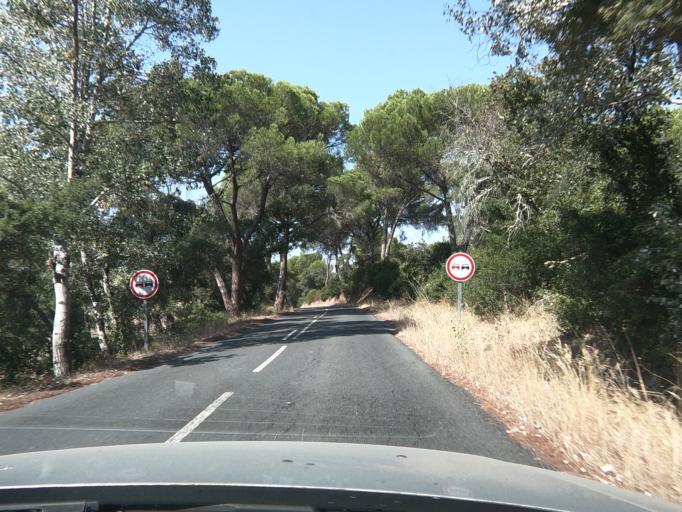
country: PT
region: Setubal
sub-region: Alcacer do Sal
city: Alcacer do Sal
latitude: 38.3077
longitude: -8.4268
